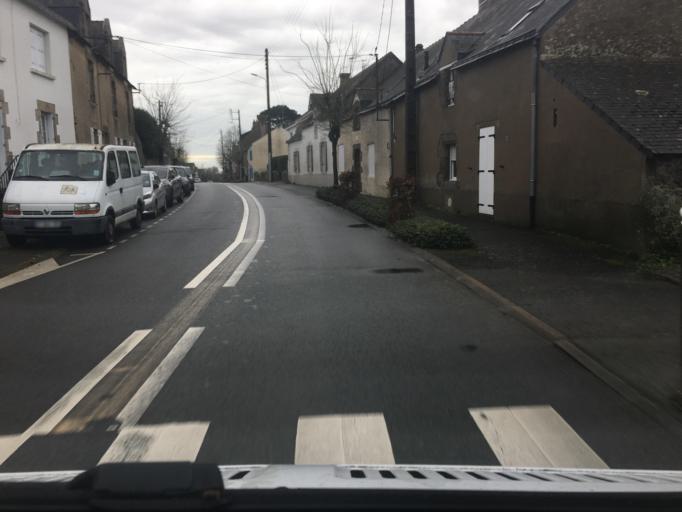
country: FR
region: Pays de la Loire
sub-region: Departement de la Loire-Atlantique
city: Guerande
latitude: 47.3235
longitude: -2.4290
